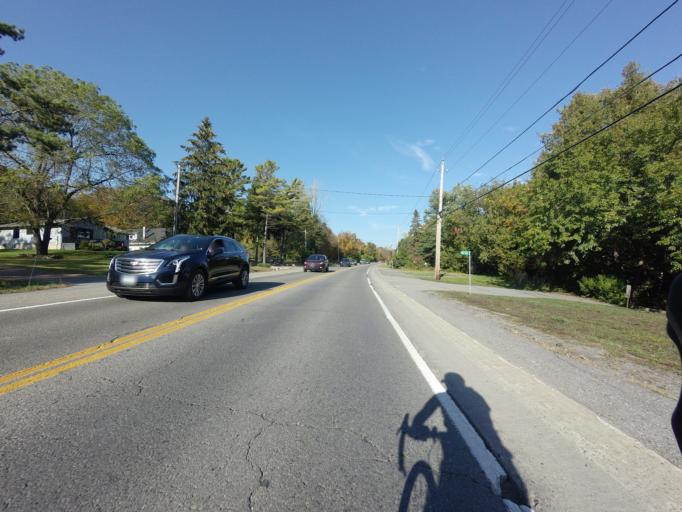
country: CA
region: Ontario
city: Kingston
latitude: 44.2332
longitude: -76.6242
